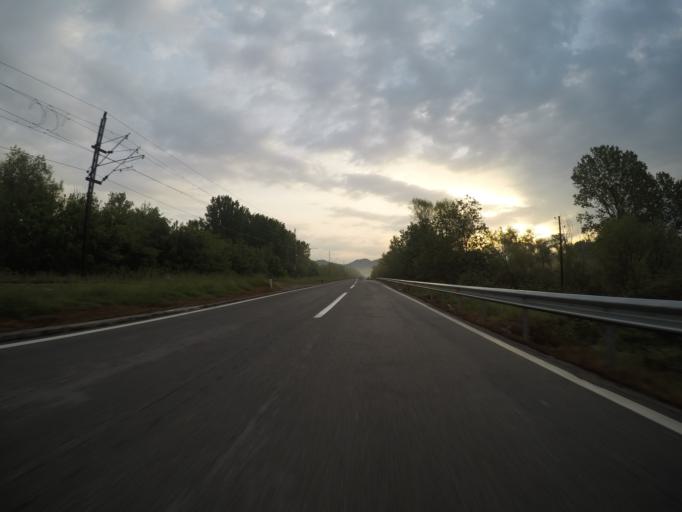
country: ME
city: Mojanovici
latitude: 42.2976
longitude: 19.1617
